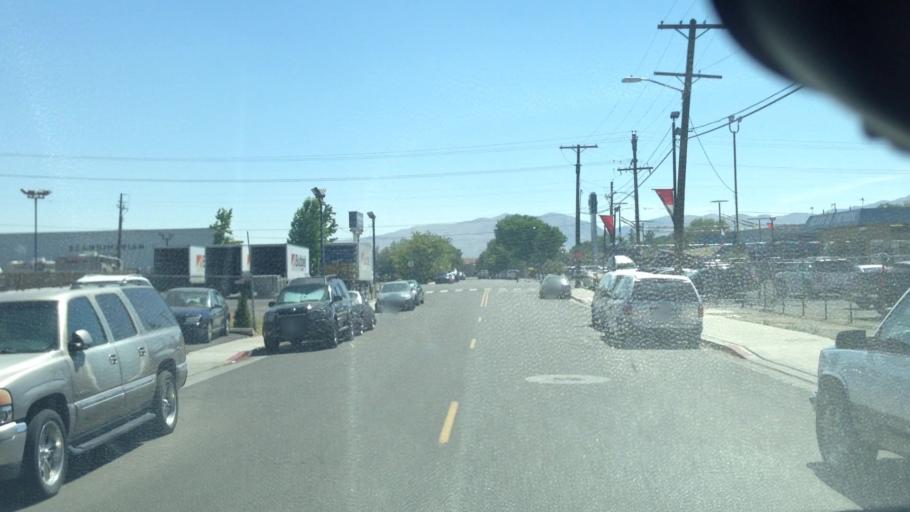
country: US
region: Nevada
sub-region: Washoe County
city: Reno
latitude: 39.4996
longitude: -119.7903
